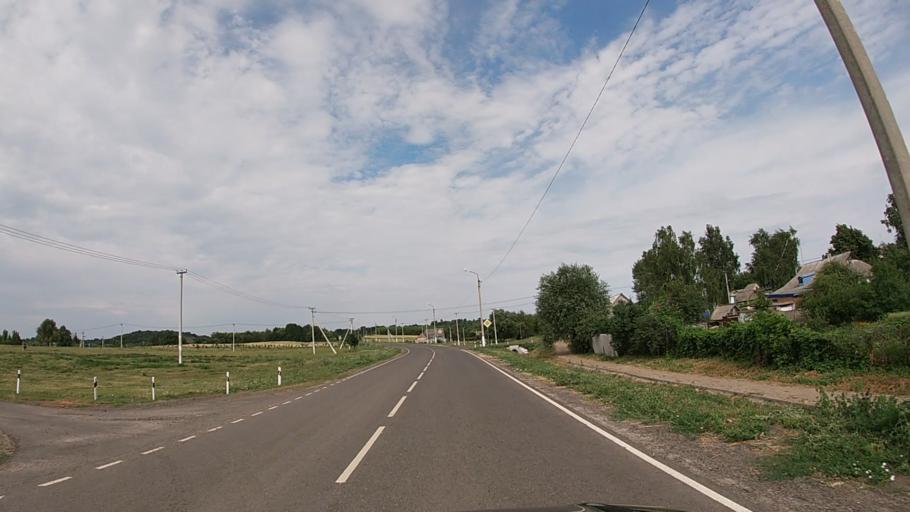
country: UA
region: Sumy
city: Krasnopillya
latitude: 50.8146
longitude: 35.4367
